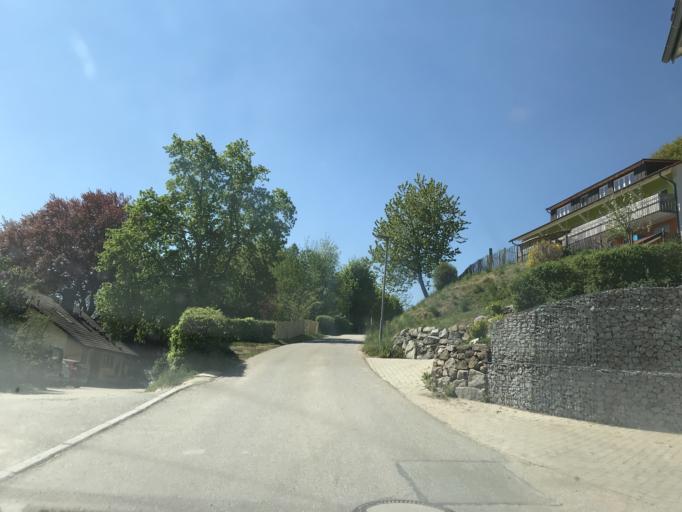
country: DE
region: Baden-Wuerttemberg
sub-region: Freiburg Region
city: Hasel
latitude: 47.6824
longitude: 7.8819
